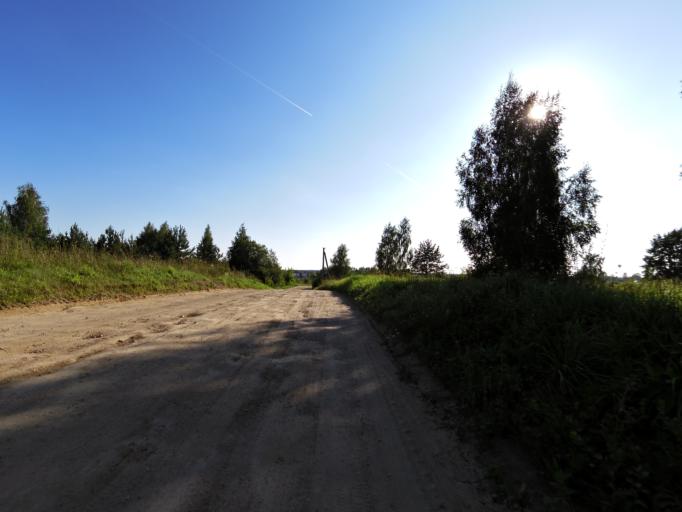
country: LT
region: Vilnius County
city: Pilaite
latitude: 54.7131
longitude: 25.1753
